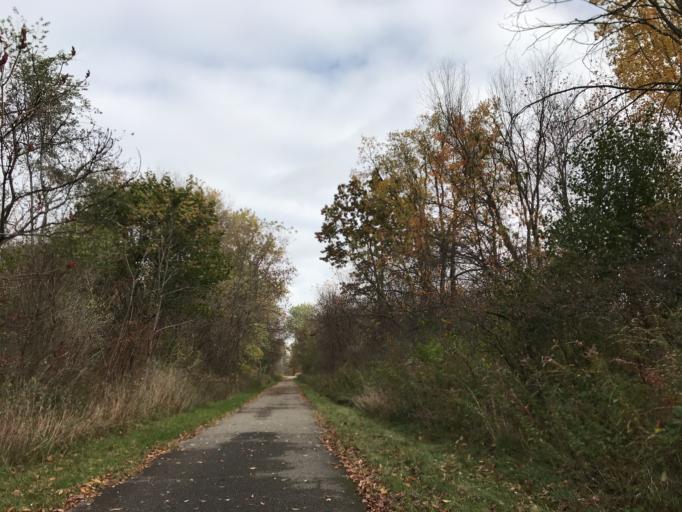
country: US
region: Michigan
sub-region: Oakland County
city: South Lyon
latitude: 42.4974
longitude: -83.6226
